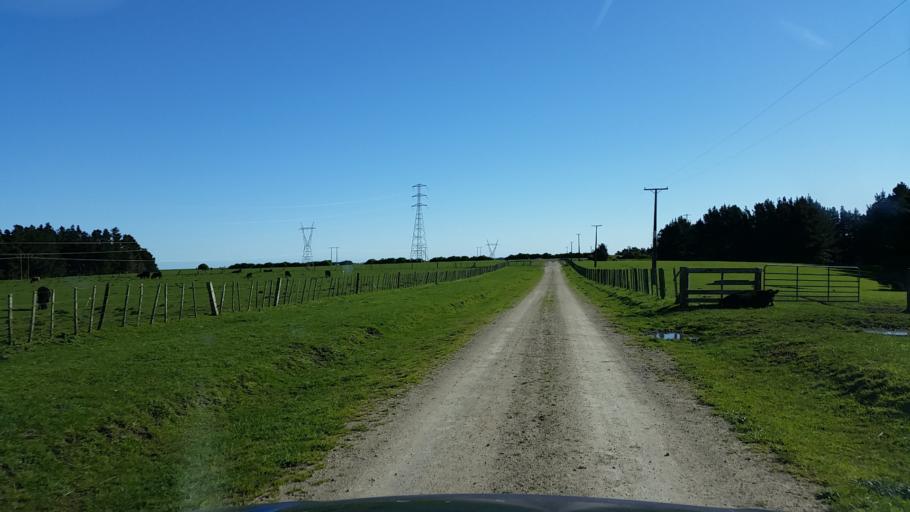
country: NZ
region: Taranaki
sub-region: South Taranaki District
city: Patea
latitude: -39.7892
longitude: 174.7533
